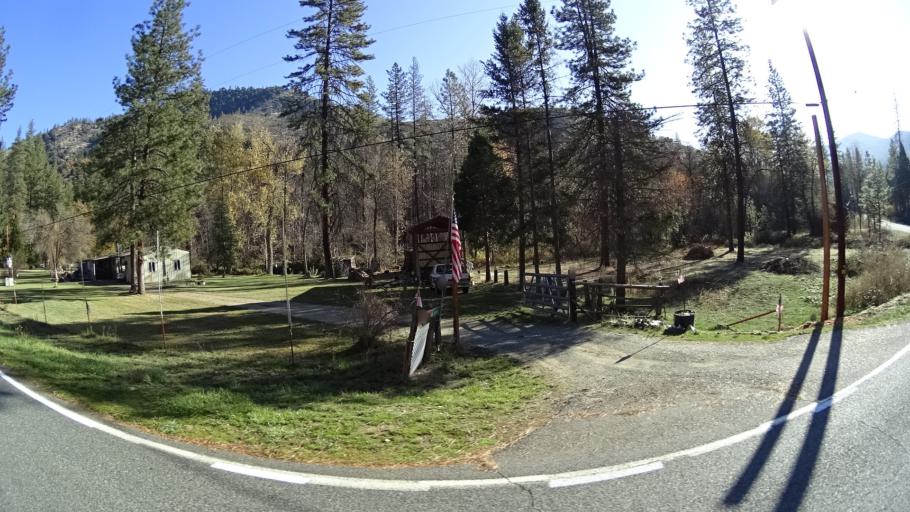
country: US
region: California
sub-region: Siskiyou County
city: Yreka
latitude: 41.8769
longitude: -122.8220
